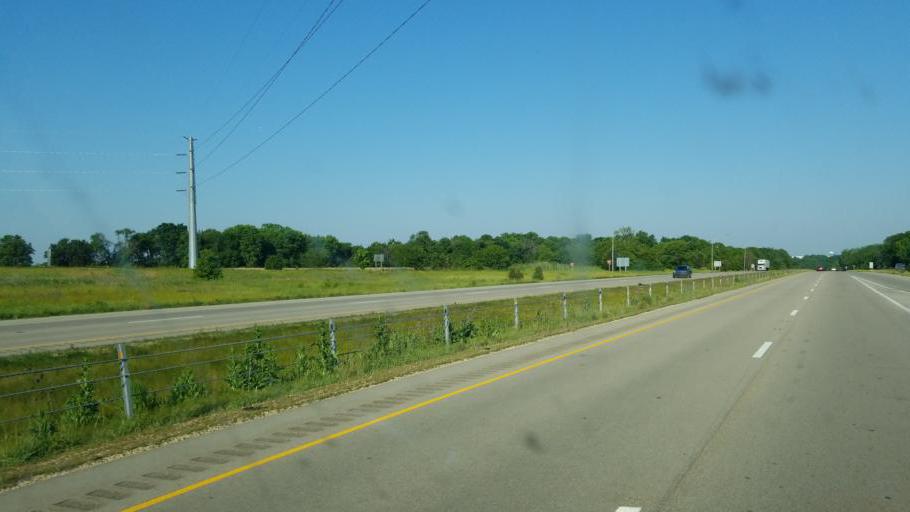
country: US
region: Illinois
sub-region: LaSalle County
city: Ottawa
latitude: 41.3767
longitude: -88.7805
